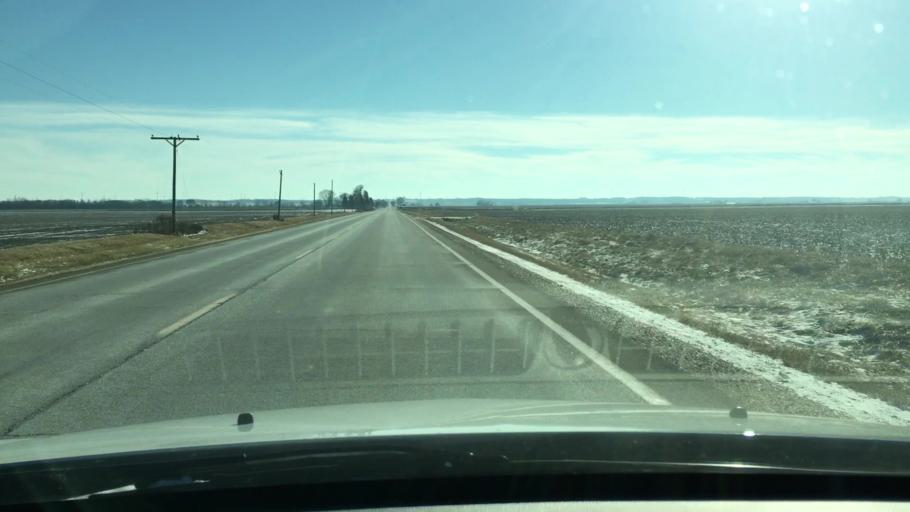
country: US
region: Illinois
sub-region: Ogle County
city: Rochelle
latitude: 41.7928
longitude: -89.0836
